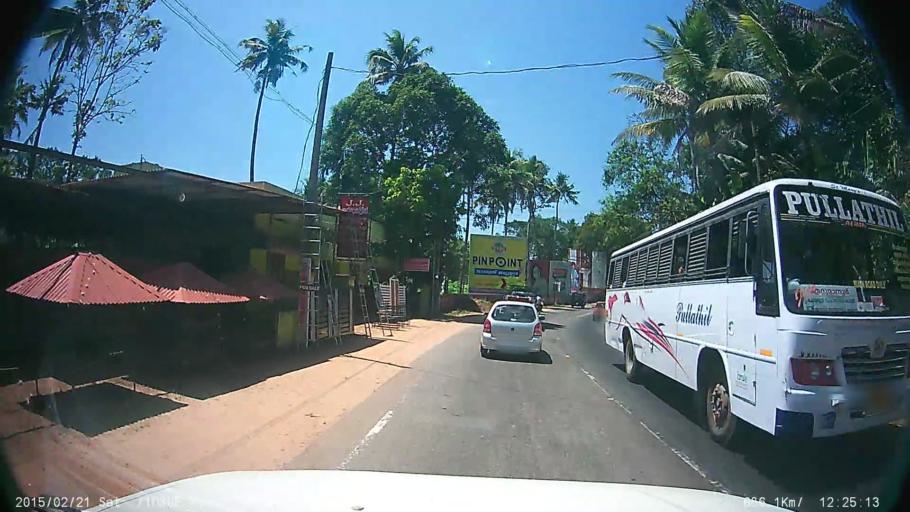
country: IN
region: Kerala
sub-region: Kottayam
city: Palackattumala
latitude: 9.6684
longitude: 76.5765
